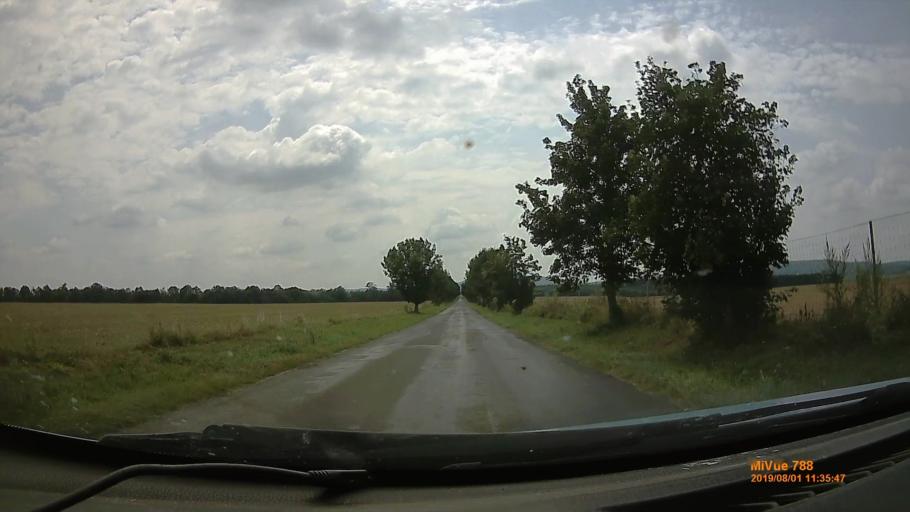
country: HU
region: Baranya
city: Villany
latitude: 45.9239
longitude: 18.3704
